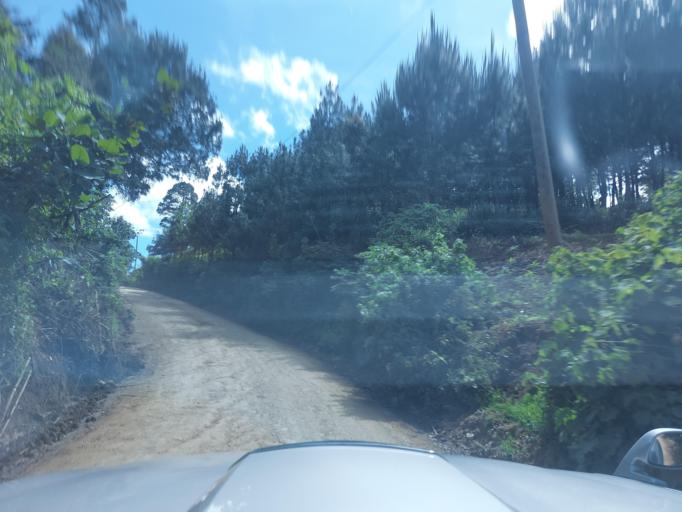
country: GT
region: Chimaltenango
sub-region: Municipio de San Juan Comalapa
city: Comalapa
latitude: 14.7575
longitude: -90.8871
